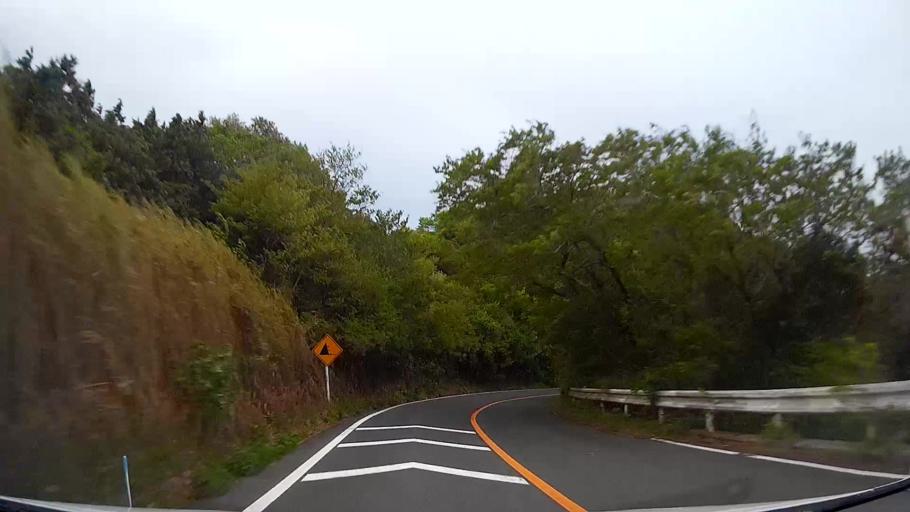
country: JP
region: Kanagawa
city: Yugawara
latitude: 35.1748
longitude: 139.0671
